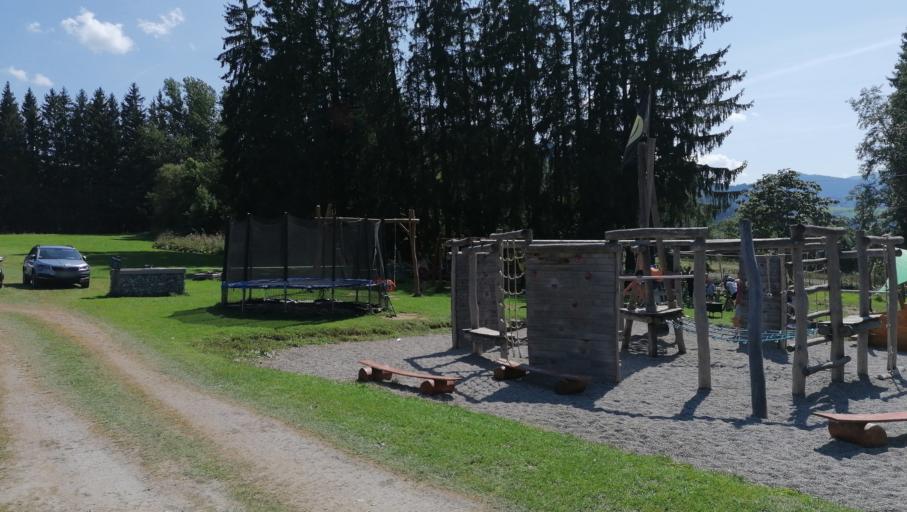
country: DE
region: Bavaria
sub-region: Swabia
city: Oy-Mittelberg
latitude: 47.6221
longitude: 10.4573
